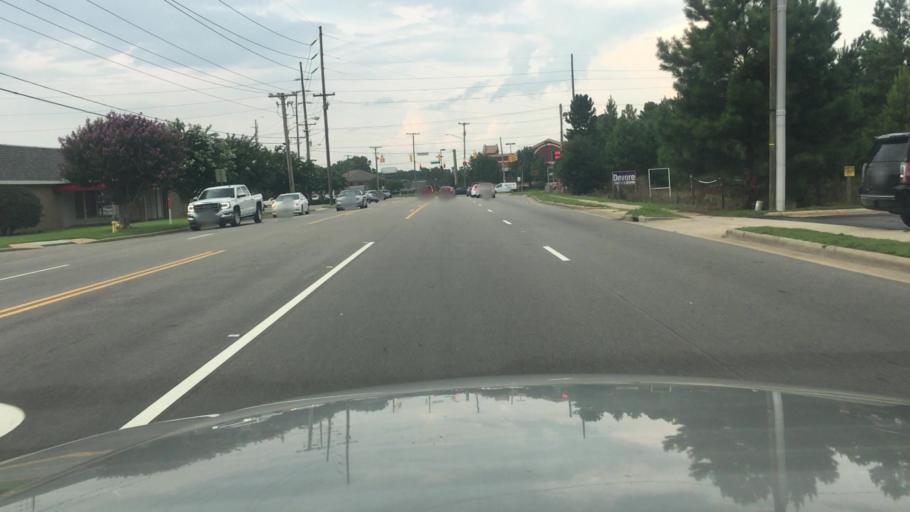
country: US
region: North Carolina
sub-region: Cumberland County
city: Fayetteville
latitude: 35.0658
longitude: -78.9507
